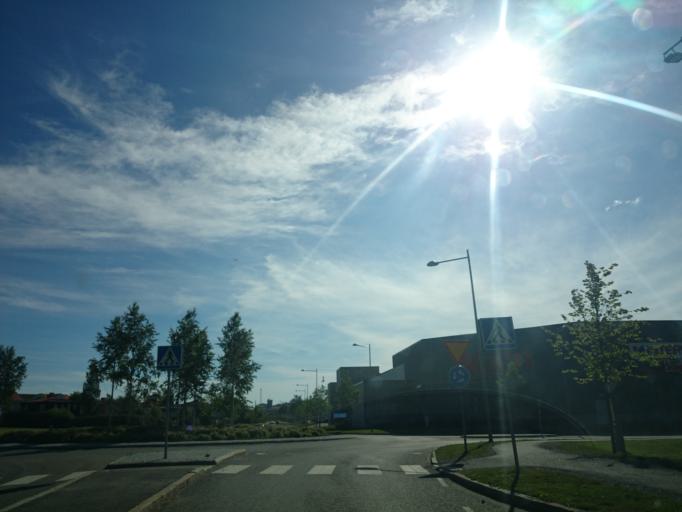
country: SE
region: Vaesternorrland
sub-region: Haernoesands Kommun
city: Haernoesand
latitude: 62.6370
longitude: 17.9246
